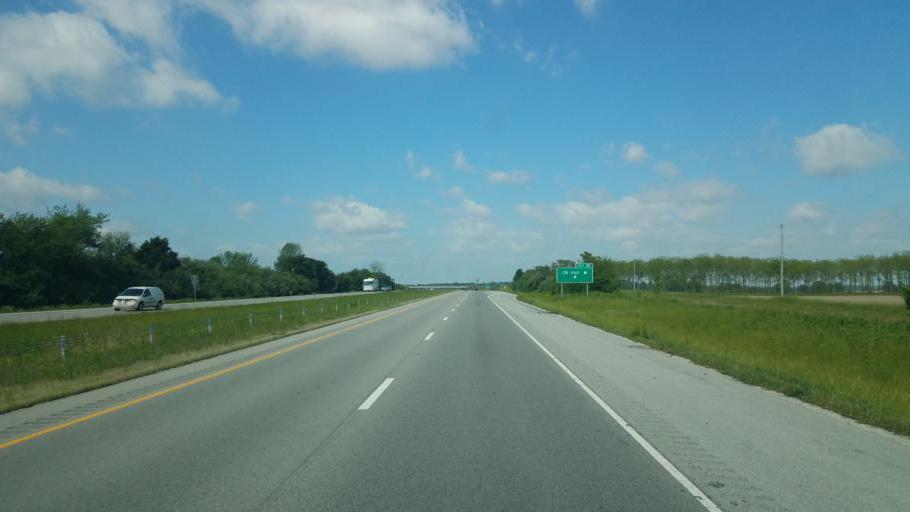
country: US
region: Indiana
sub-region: Morgan County
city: Monrovia
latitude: 39.5730
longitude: -86.6235
